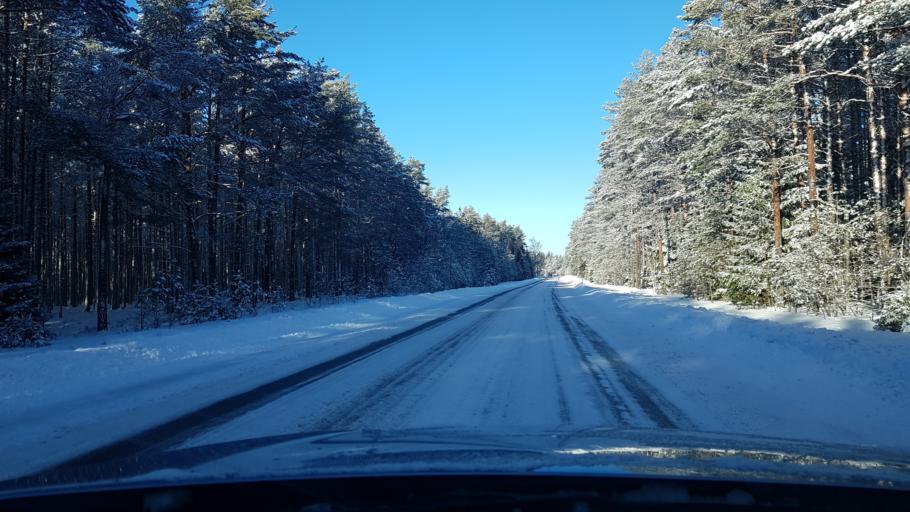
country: EE
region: Hiiumaa
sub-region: Kaerdla linn
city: Kardla
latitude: 58.9321
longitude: 22.7831
